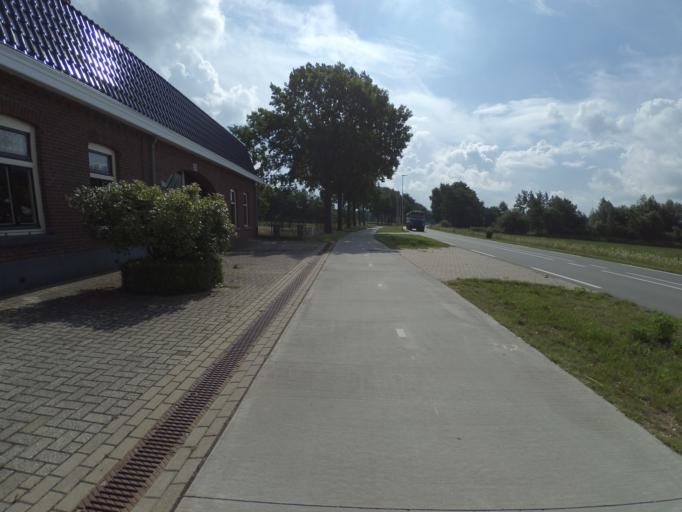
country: NL
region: Limburg
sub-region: Gemeente Roerdalen
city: Montfort
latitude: 51.0868
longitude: 5.9256
